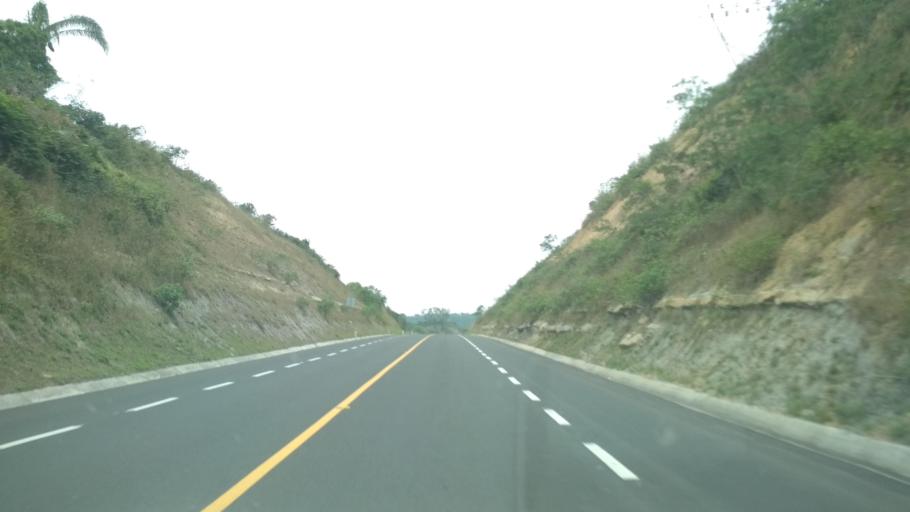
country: MX
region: Veracruz
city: Gutierrez Zamora
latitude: 20.3049
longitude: -97.0958
